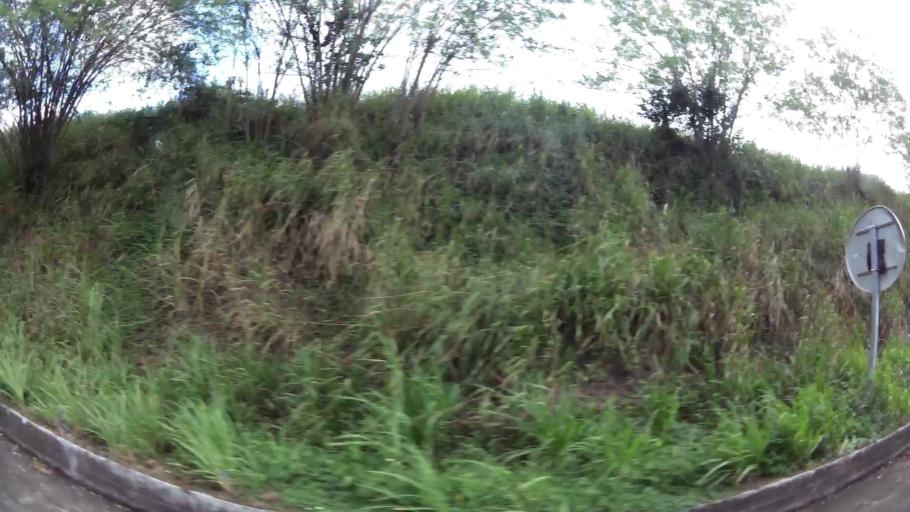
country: MQ
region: Martinique
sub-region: Martinique
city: Les Trois-Ilets
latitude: 14.5179
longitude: -60.9840
